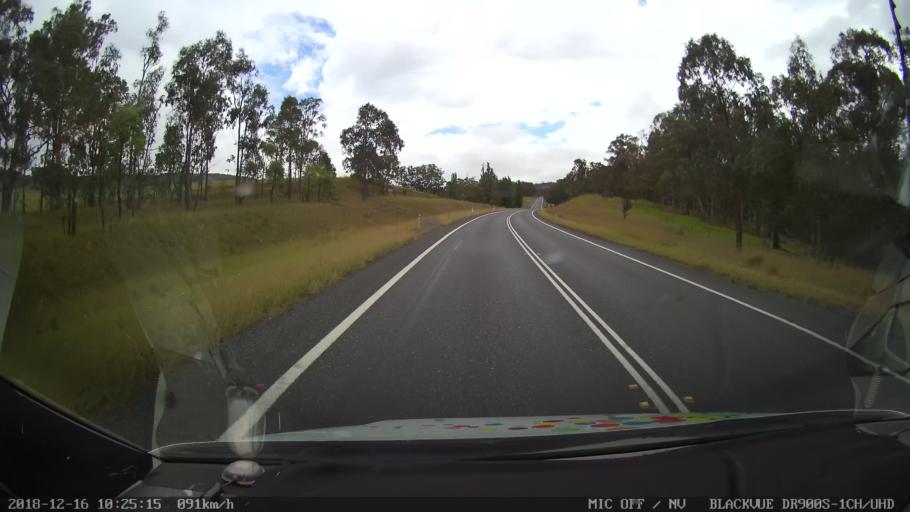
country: AU
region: New South Wales
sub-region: Tenterfield Municipality
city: Carrolls Creek
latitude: -29.1610
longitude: 152.0006
